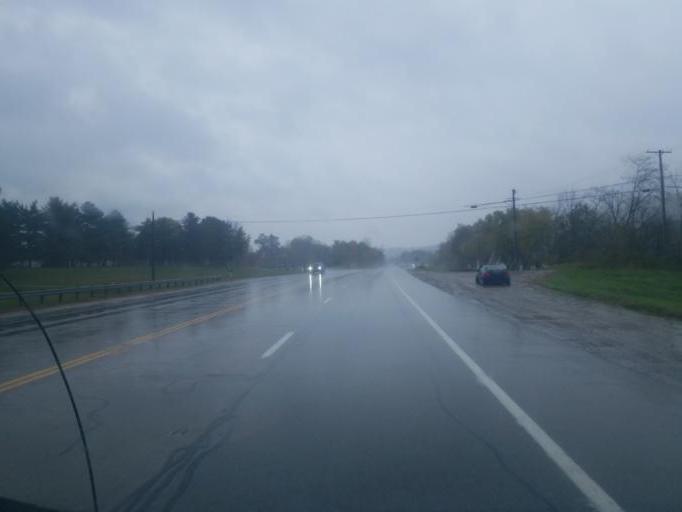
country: US
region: Ohio
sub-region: Muskingum County
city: South Zanesville
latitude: 39.8811
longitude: -81.9791
